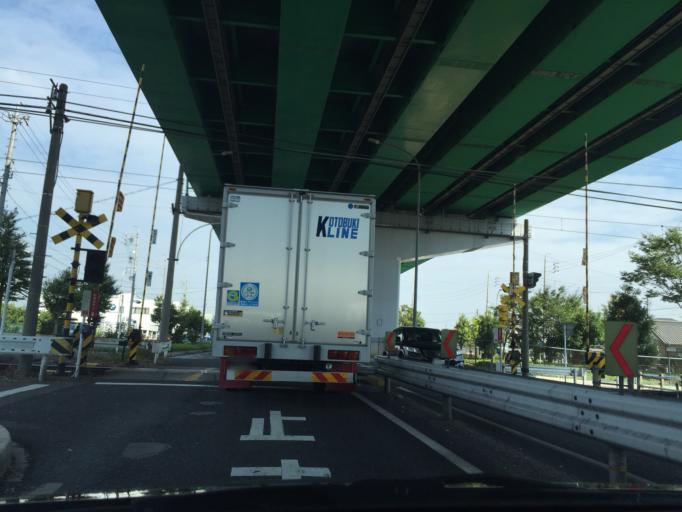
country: JP
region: Aichi
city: Ichinomiya
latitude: 35.2877
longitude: 136.7808
